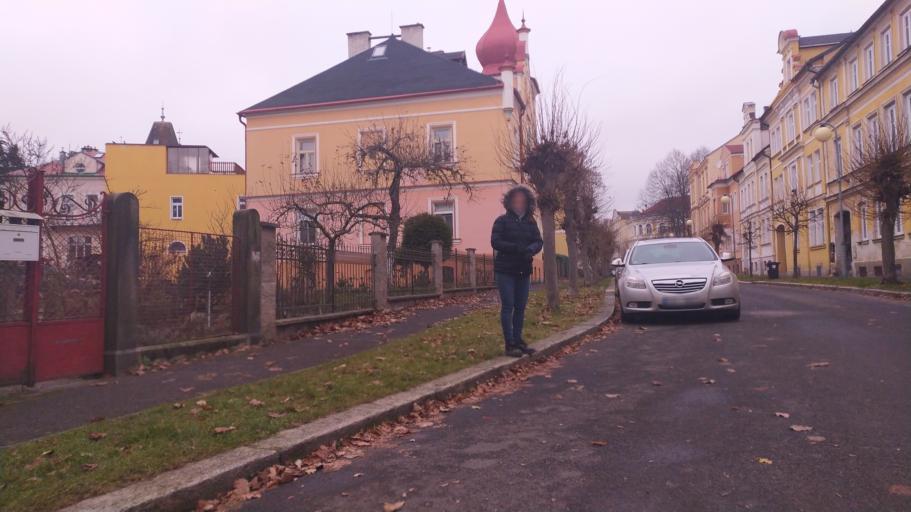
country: CZ
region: Karlovarsky
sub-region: Okres Cheb
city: Frantiskovy Lazne
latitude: 50.1223
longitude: 12.3557
